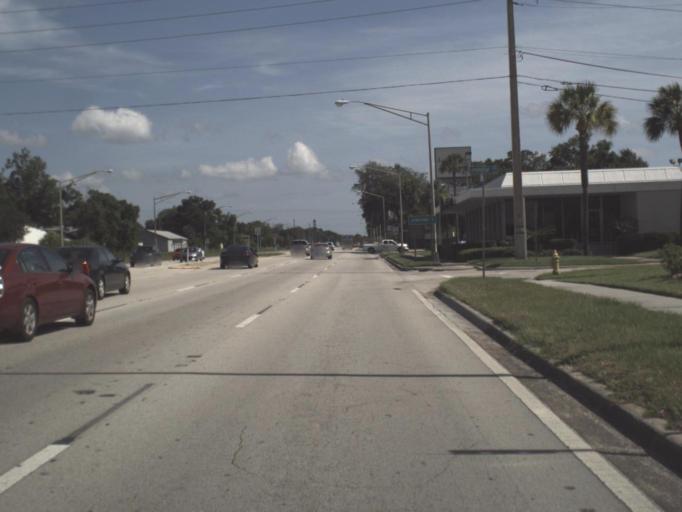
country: US
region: Florida
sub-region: Duval County
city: Jacksonville
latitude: 30.2828
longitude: -81.7201
